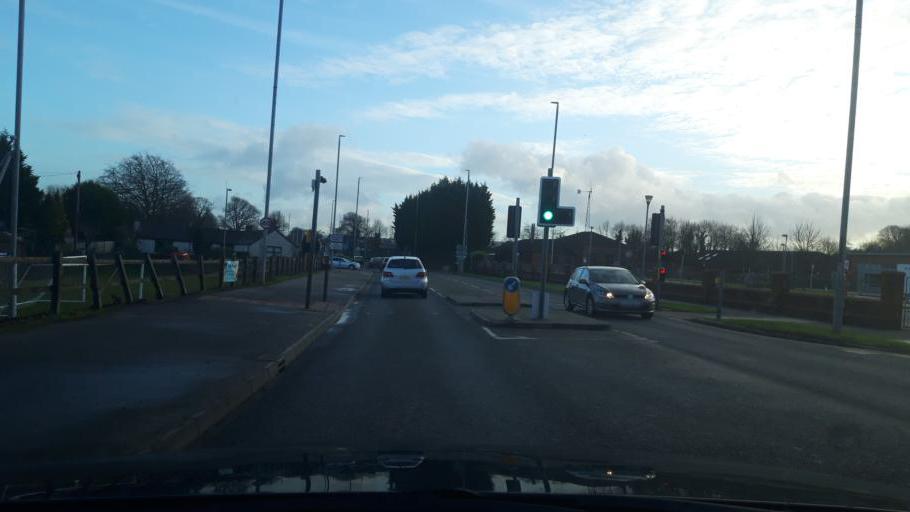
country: GB
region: Northern Ireland
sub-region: Dungannon District
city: Dungannon
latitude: 54.4890
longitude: -6.7475
